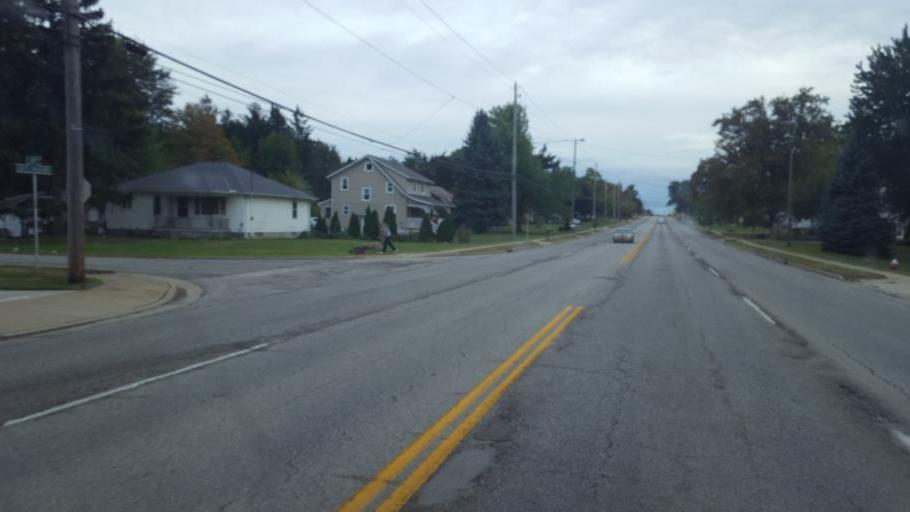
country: US
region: Ohio
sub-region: Lorain County
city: Lorain
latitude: 41.4303
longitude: -82.1626
